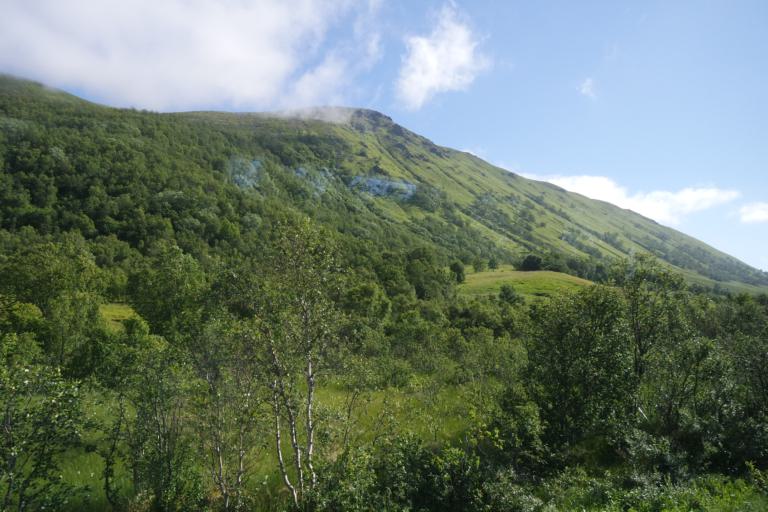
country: NO
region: Nordland
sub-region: Sortland
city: Sortland
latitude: 69.0042
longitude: 15.6073
